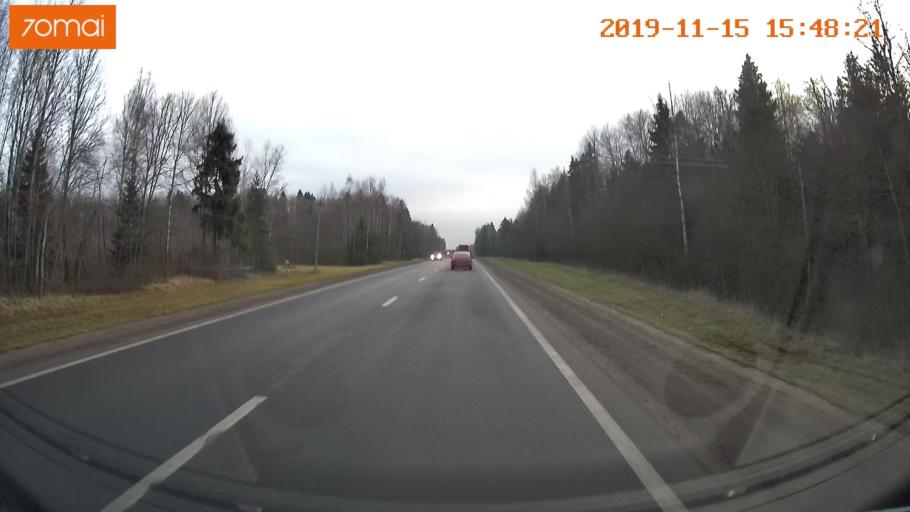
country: RU
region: Jaroslavl
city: Danilov
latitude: 57.9283
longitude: 40.0065
